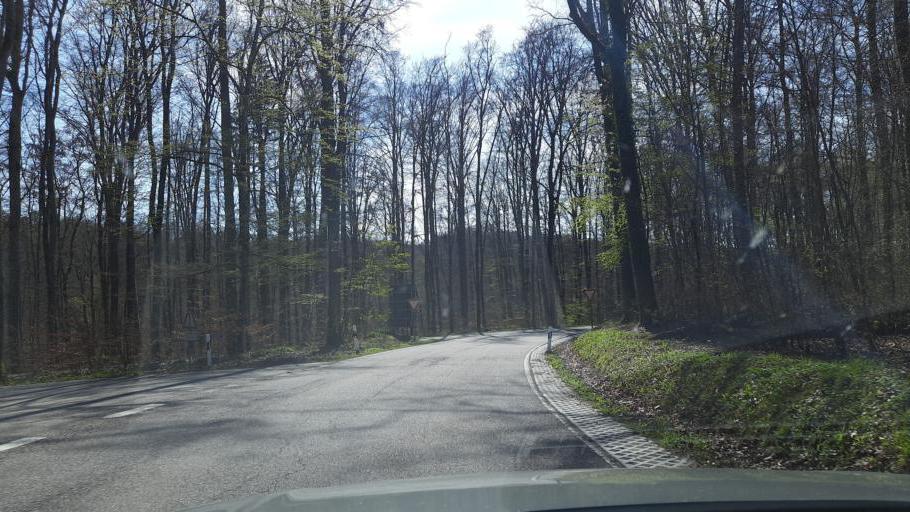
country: DE
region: Baden-Wuerttemberg
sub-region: Regierungsbezirk Stuttgart
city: Widdern
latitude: 49.2775
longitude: 9.3891
